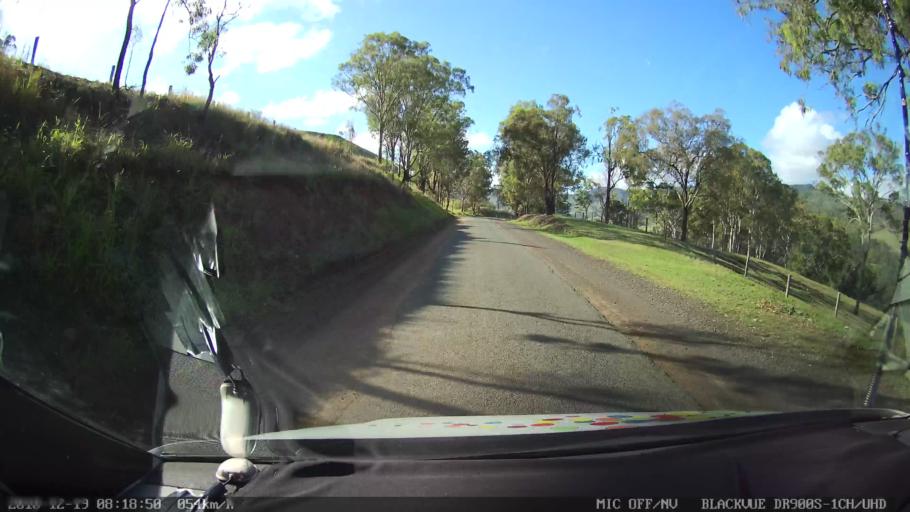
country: AU
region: New South Wales
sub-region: Kyogle
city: Kyogle
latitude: -28.2766
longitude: 152.9091
